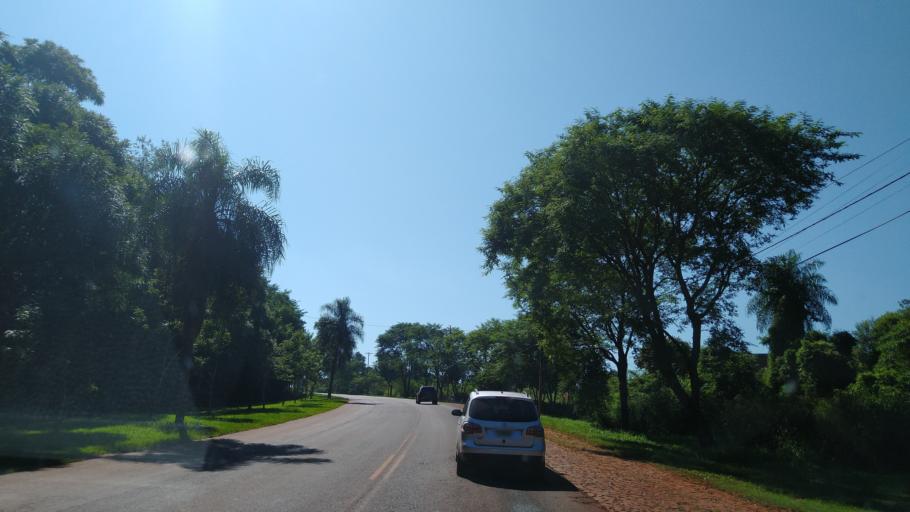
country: AR
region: Misiones
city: Puerto Esperanza
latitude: -26.0222
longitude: -54.6005
